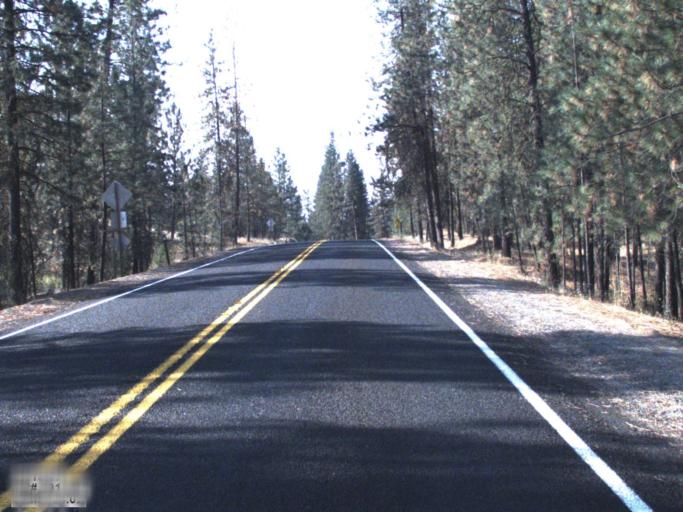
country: US
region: Washington
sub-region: Spokane County
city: Deer Park
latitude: 47.8785
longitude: -117.7071
